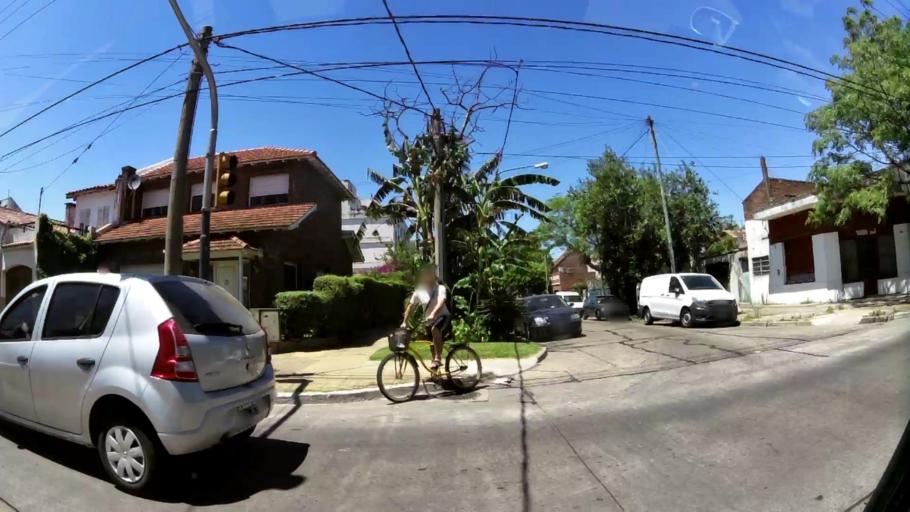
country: AR
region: Buenos Aires
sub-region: Partido de Vicente Lopez
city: Olivos
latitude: -34.5016
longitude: -58.5062
